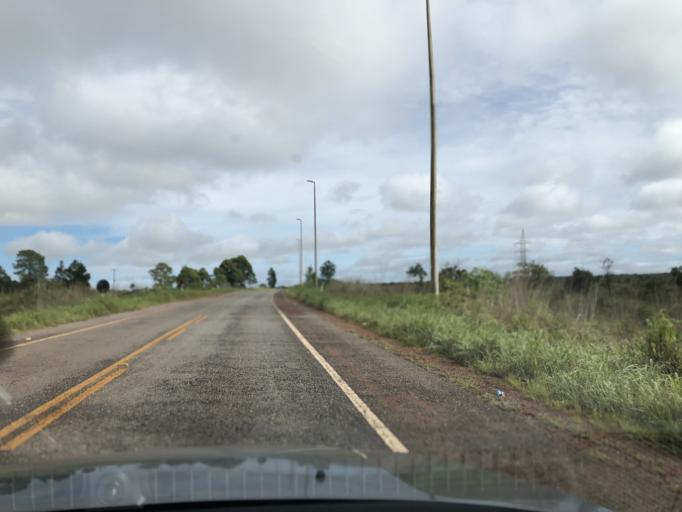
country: BR
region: Federal District
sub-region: Brasilia
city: Brasilia
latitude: -15.7268
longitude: -48.0855
